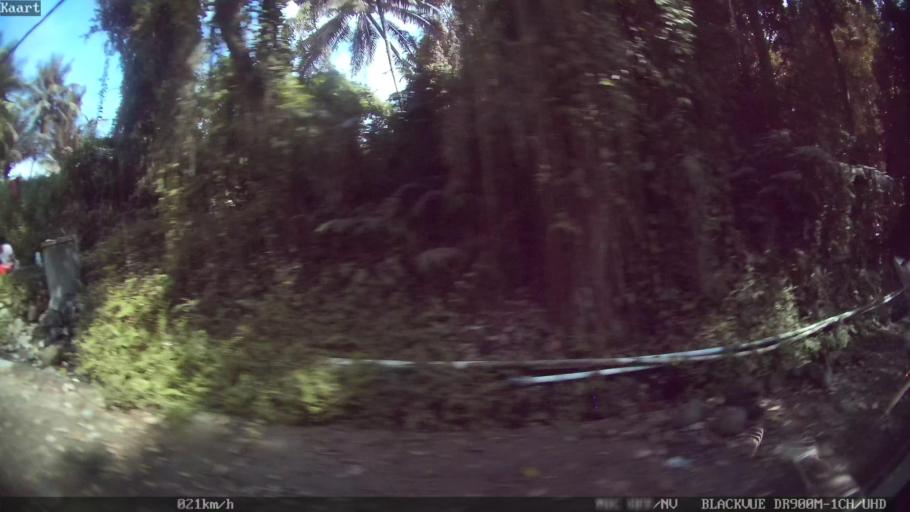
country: ID
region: Bali
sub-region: Kabupaten Gianyar
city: Ubud
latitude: -8.5114
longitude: 115.2890
